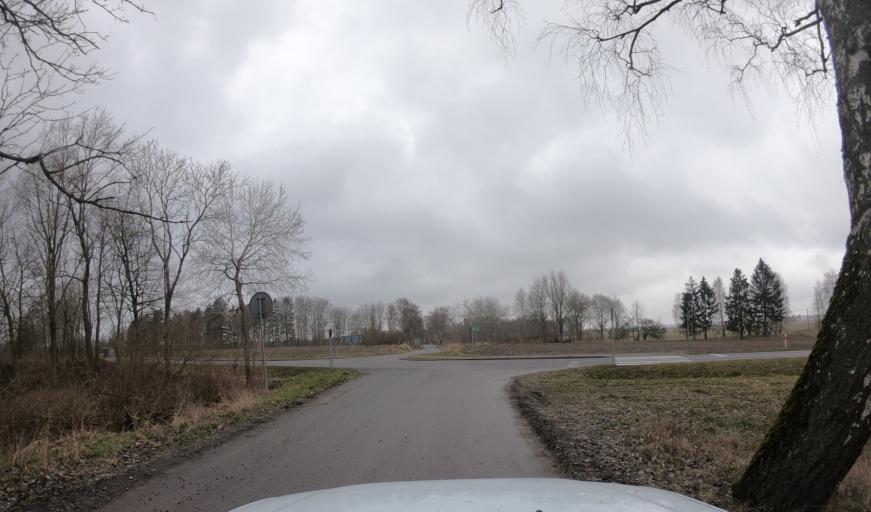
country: PL
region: West Pomeranian Voivodeship
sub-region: Powiat kamienski
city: Swierzno
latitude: 53.9584
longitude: 14.9183
